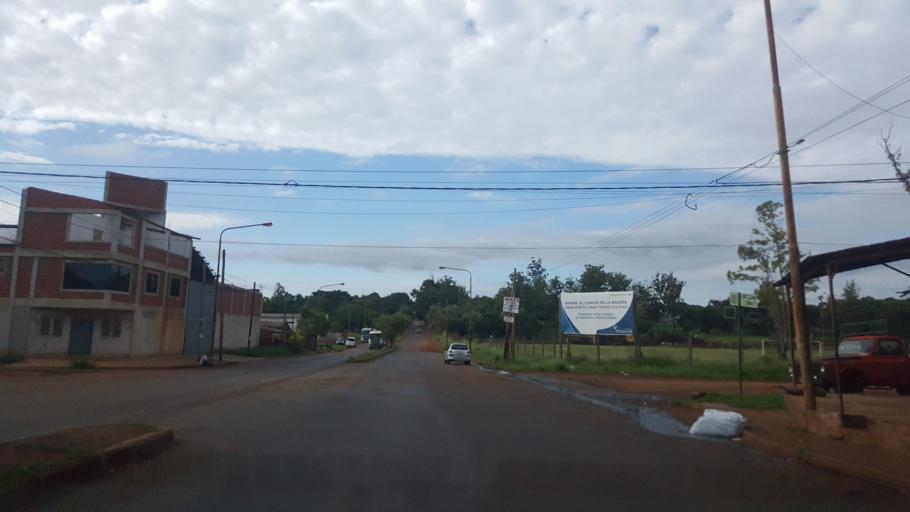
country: AR
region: Misiones
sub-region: Departamento de Capital
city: Posadas
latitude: -27.3943
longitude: -55.9355
